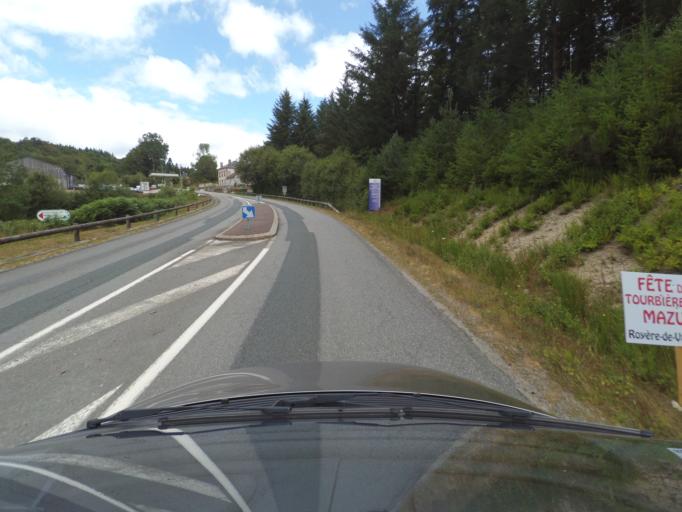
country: FR
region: Limousin
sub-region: Departement de la Haute-Vienne
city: Peyrat-le-Chateau
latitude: 45.8373
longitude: 1.9129
